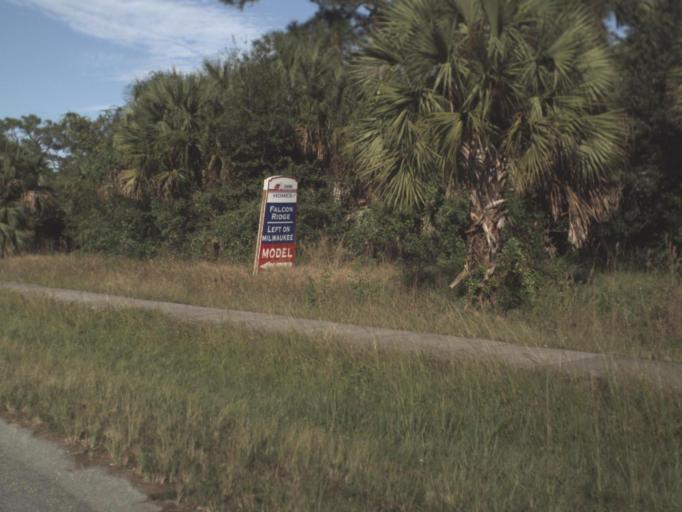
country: US
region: Florida
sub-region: Brevard County
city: June Park
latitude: 28.0689
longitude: -80.6707
